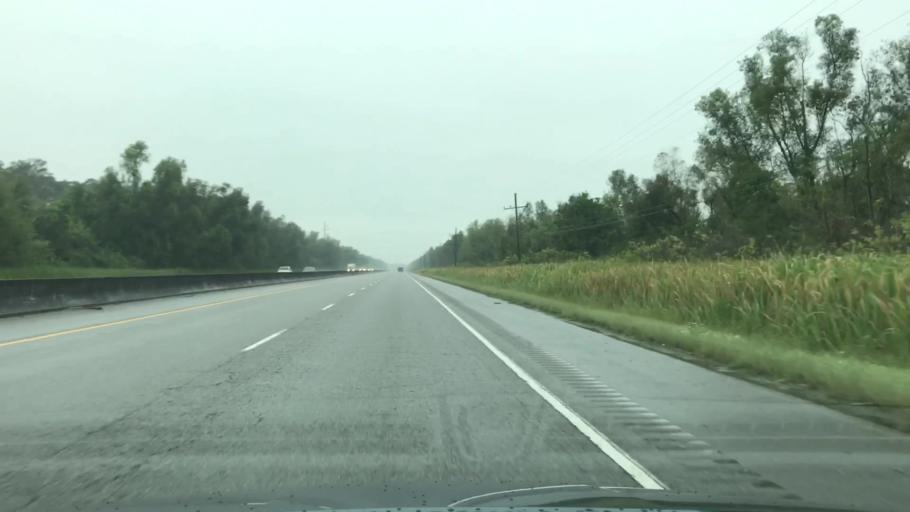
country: US
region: Louisiana
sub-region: Saint Charles Parish
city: Des Allemands
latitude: 29.7742
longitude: -90.5345
